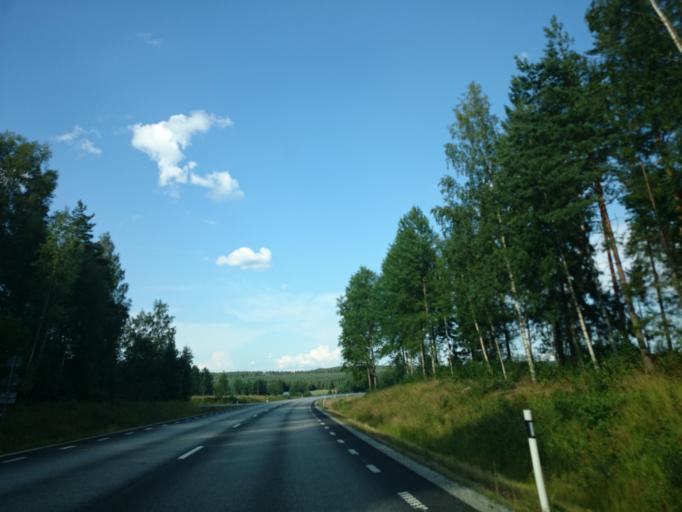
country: SE
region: OErebro
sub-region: Lindesbergs Kommun
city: Lindesberg
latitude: 59.7475
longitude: 15.4327
